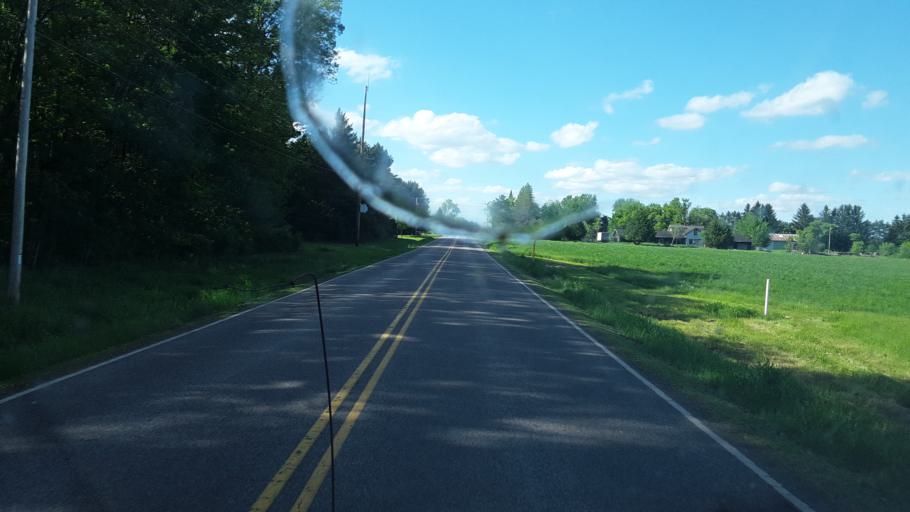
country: US
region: Wisconsin
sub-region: Wood County
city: Marshfield
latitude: 44.4507
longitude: -90.1610
